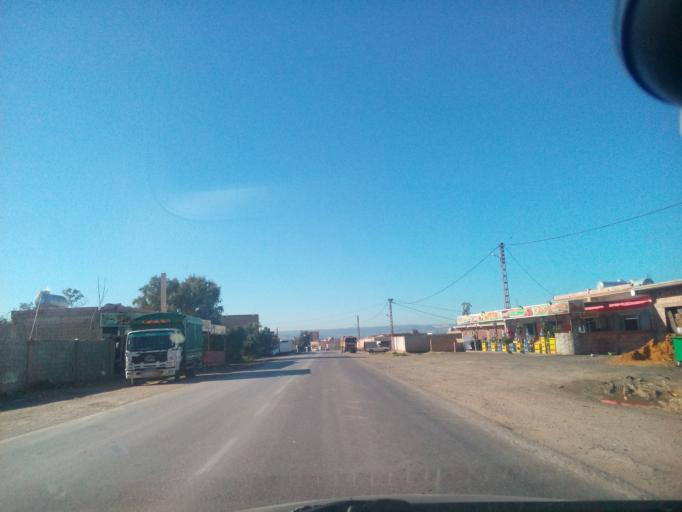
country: DZ
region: Relizane
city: Relizane
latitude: 35.8974
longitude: 0.5912
